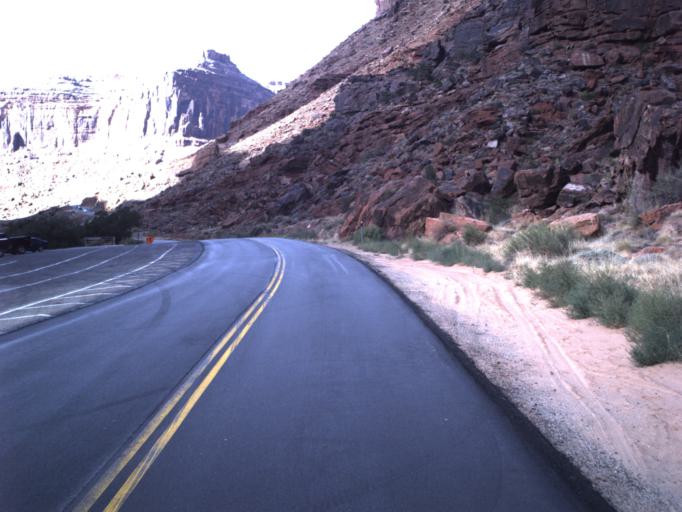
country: US
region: Utah
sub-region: Grand County
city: Moab
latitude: 38.6613
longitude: -109.5002
